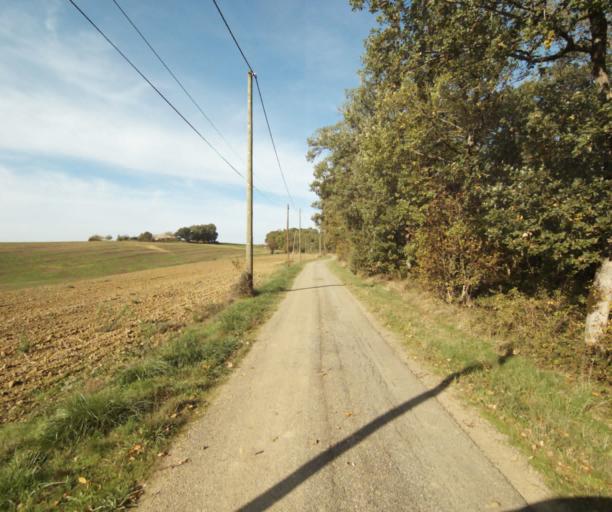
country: FR
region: Midi-Pyrenees
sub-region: Departement du Tarn-et-Garonne
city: Nohic
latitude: 43.9260
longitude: 1.4708
